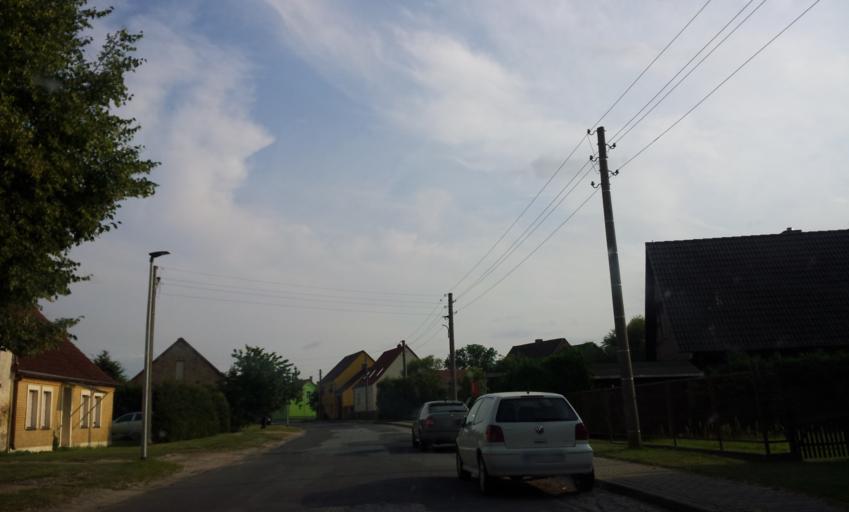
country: DE
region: Brandenburg
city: Treuenbrietzen
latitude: 52.0789
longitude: 12.9429
